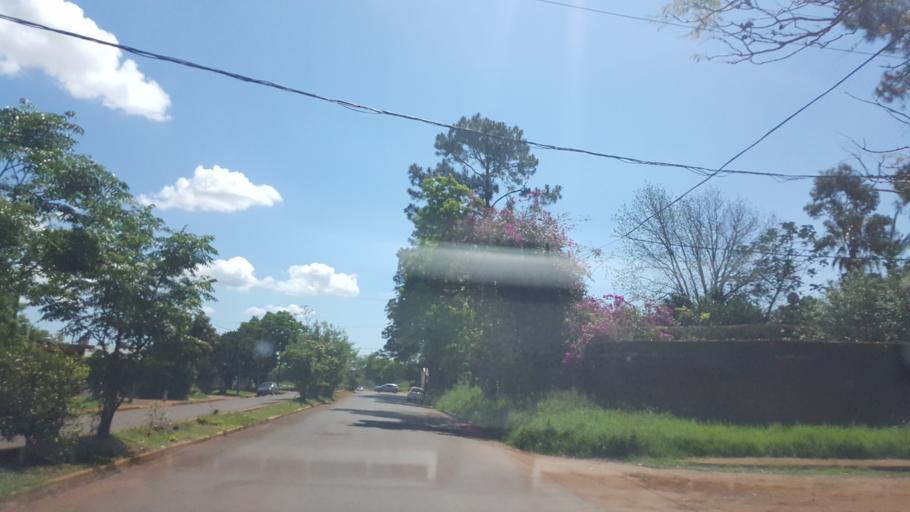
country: AR
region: Misiones
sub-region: Departamento de Capital
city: Posadas
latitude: -27.3798
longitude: -55.9398
